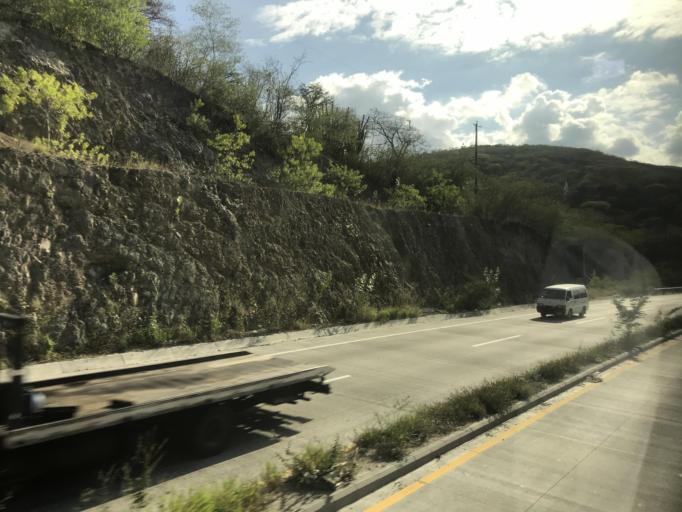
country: GT
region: El Progreso
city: Guastatoya
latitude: 14.8548
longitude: -90.0917
